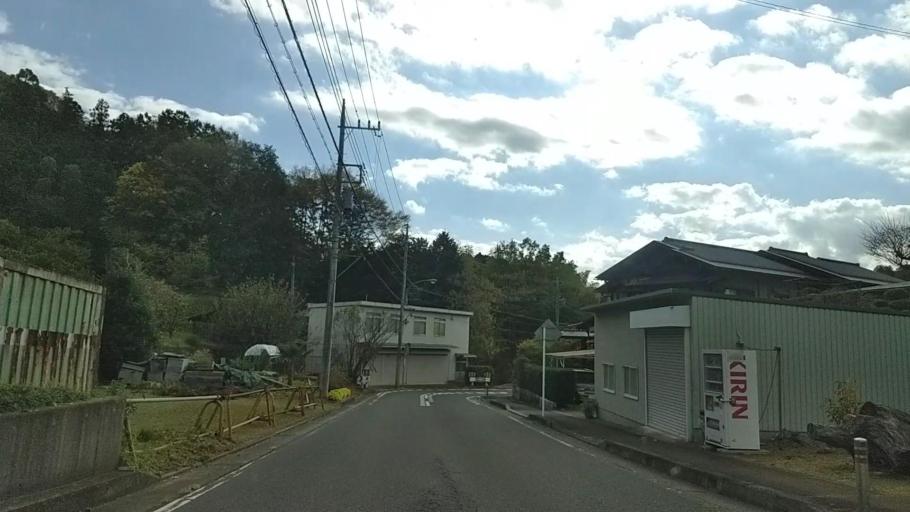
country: JP
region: Kanagawa
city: Hadano
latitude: 35.3533
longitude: 139.1703
